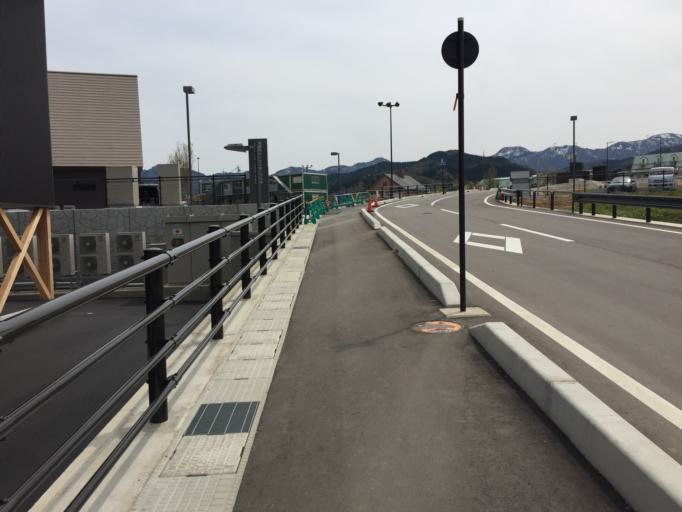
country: JP
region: Toyama
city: Fukumitsu
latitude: 36.5022
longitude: 136.8725
